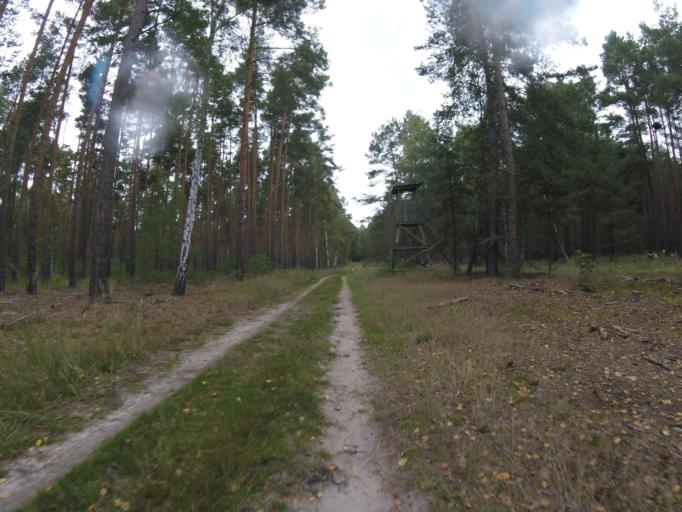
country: DE
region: Brandenburg
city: Gross Koris
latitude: 52.1936
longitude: 13.6744
